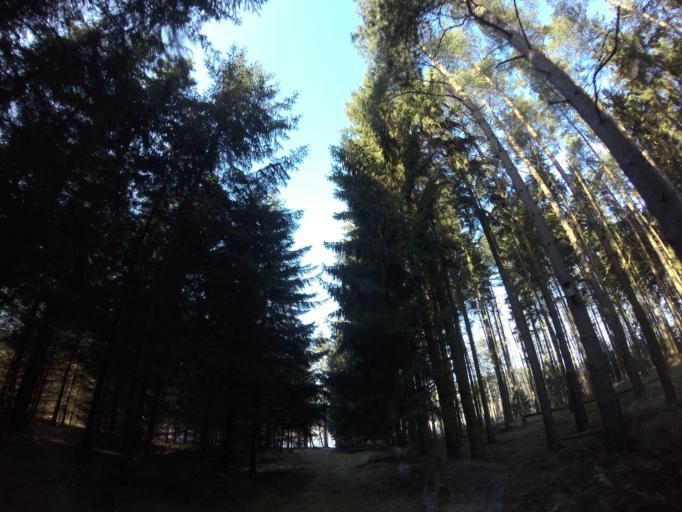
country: PL
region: West Pomeranian Voivodeship
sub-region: Powiat choszczenski
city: Pelczyce
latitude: 52.9792
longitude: 15.3683
